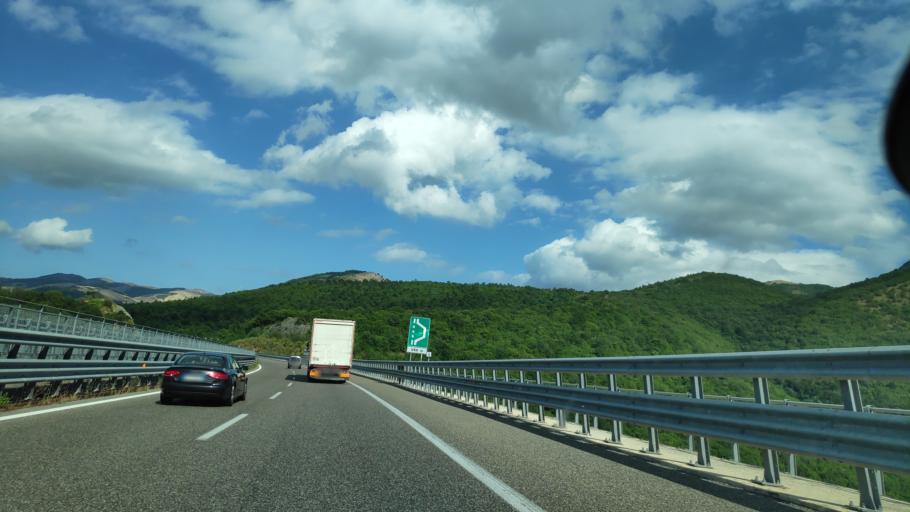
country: IT
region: Campania
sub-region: Provincia di Salerno
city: Pertosa
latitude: 40.5298
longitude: 15.4312
